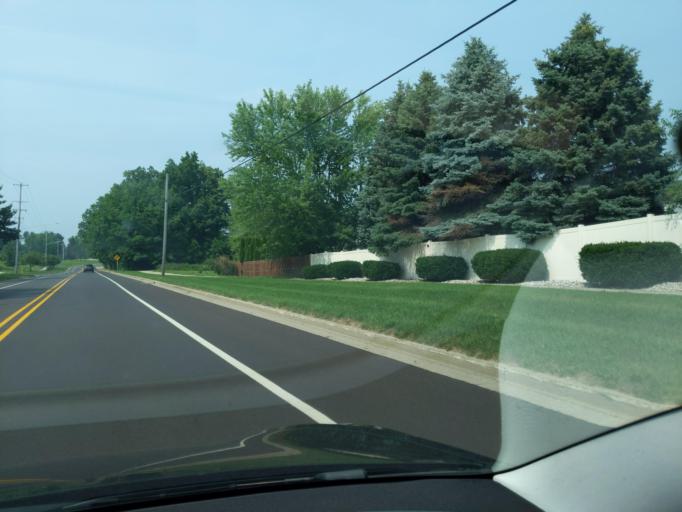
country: US
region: Michigan
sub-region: Clinton County
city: DeWitt
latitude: 42.8303
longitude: -84.5724
